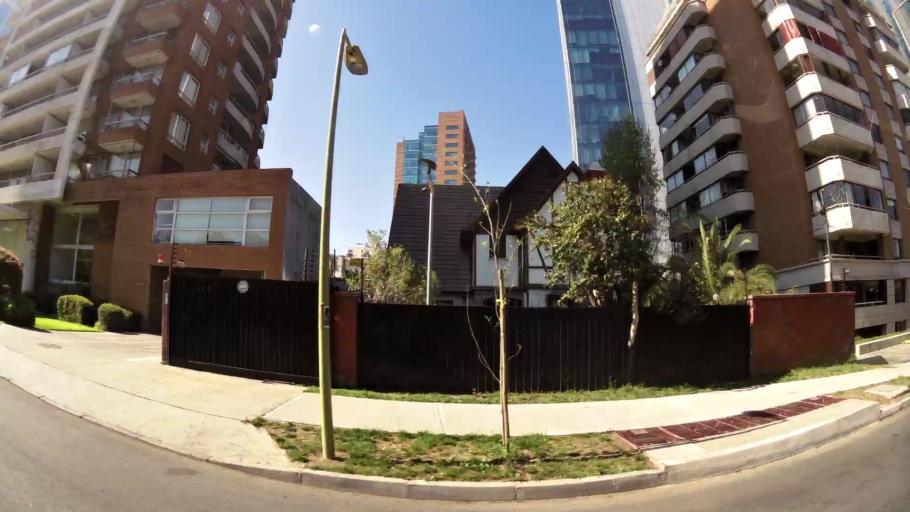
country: CL
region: Santiago Metropolitan
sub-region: Provincia de Santiago
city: Villa Presidente Frei, Nunoa, Santiago, Chile
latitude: -33.4118
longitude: -70.5807
